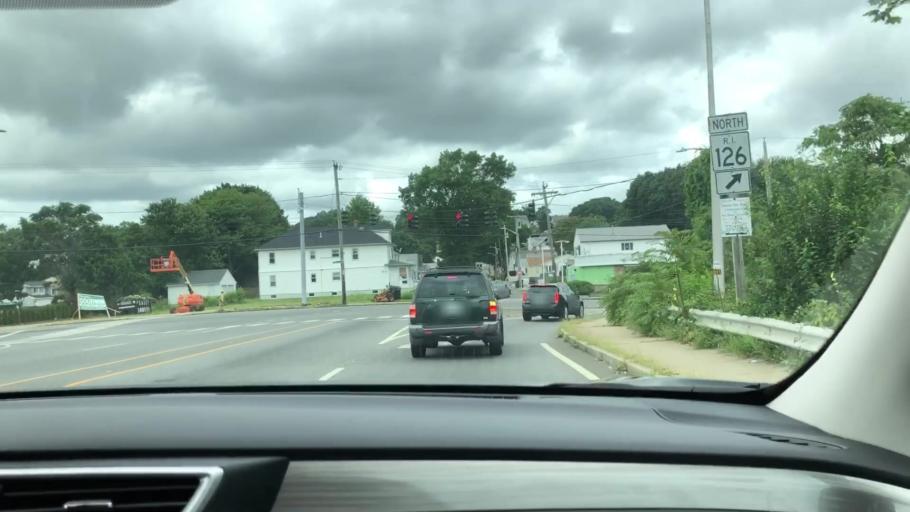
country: US
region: Rhode Island
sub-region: Providence County
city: Providence
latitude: 41.8566
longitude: -71.4102
